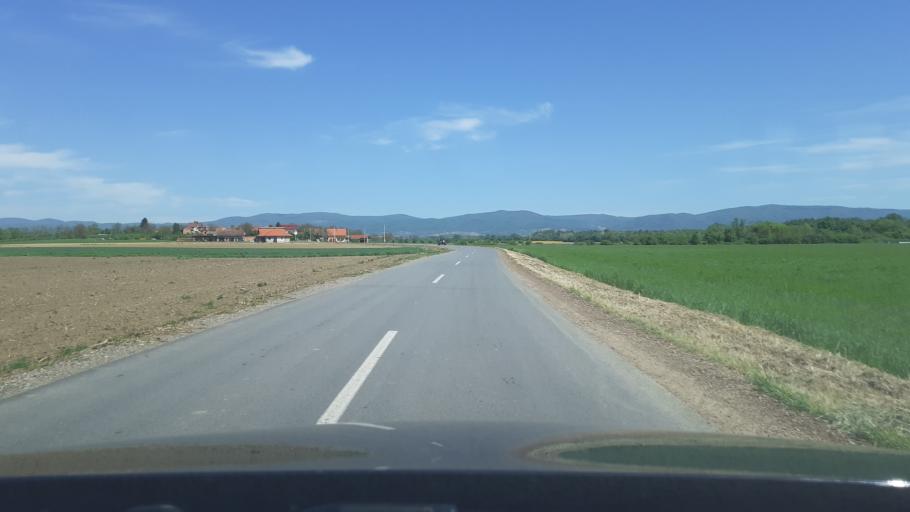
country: HR
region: Pozesko-Slavonska
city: Jaksic
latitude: 45.3563
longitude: 17.7526
